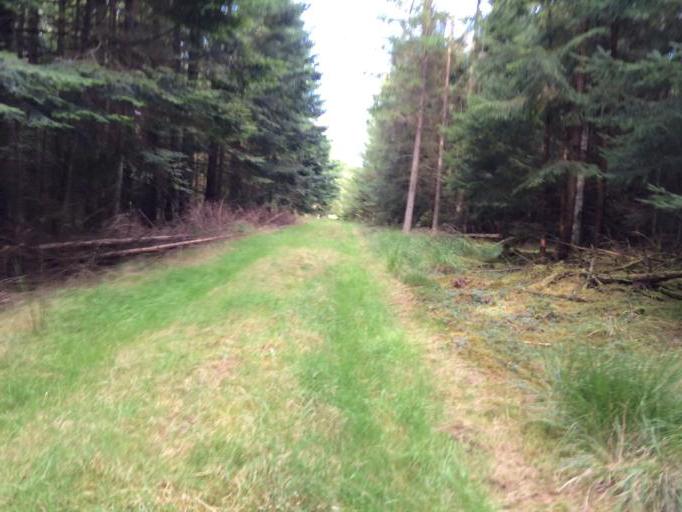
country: DK
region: Central Jutland
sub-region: Holstebro Kommune
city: Ulfborg
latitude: 56.2593
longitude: 8.4407
